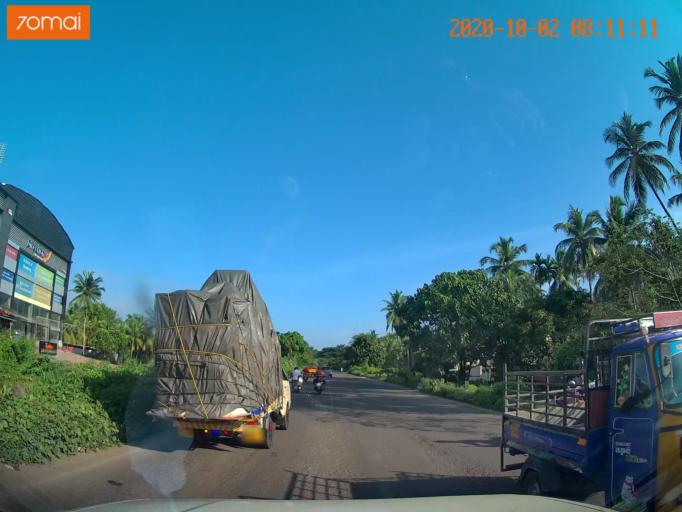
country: IN
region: Kerala
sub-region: Kozhikode
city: Kozhikode
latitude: 11.2726
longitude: 75.8086
